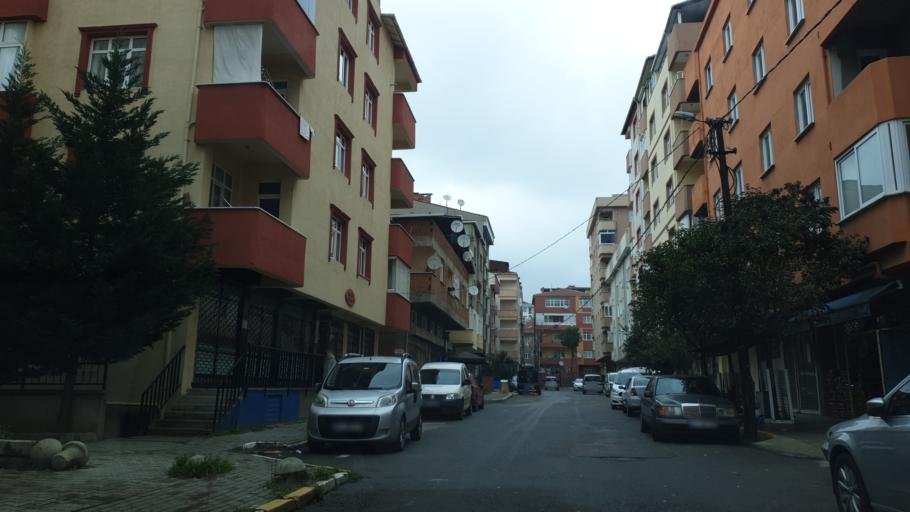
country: TR
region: Istanbul
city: Pendik
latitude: 40.8806
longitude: 29.2717
